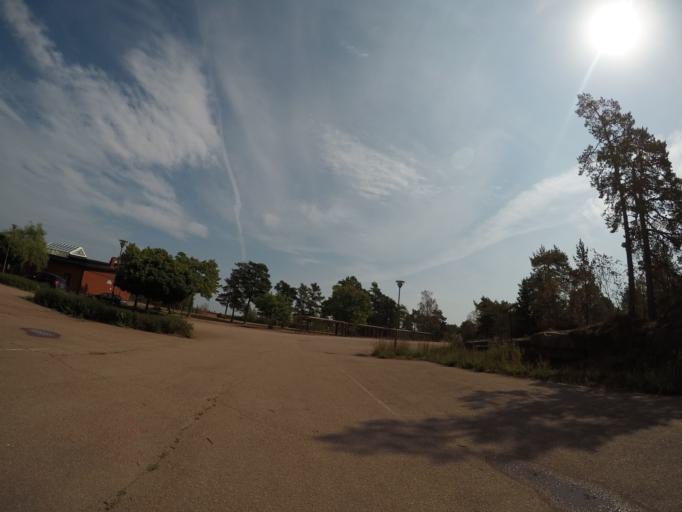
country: AX
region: Alands landsbygd
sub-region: Finstroem
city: Finstroem
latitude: 60.2237
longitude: 19.9757
